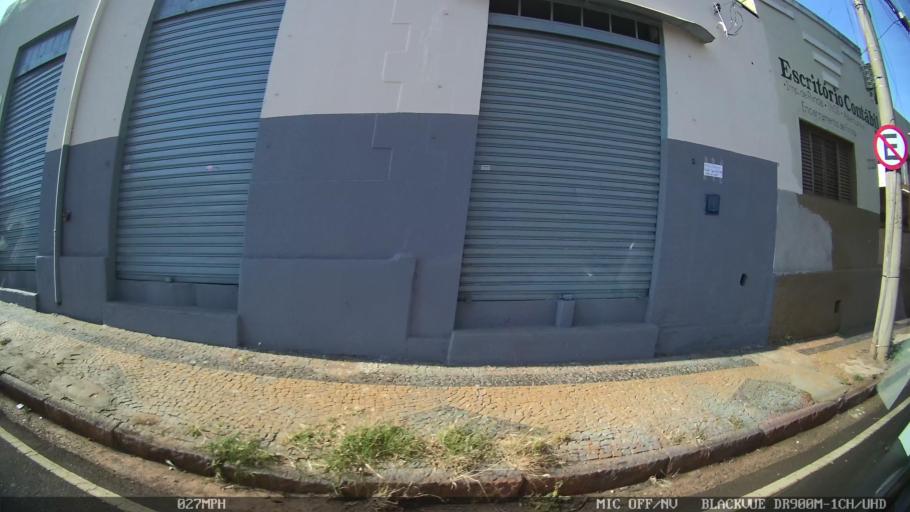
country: BR
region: Sao Paulo
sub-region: Sao Jose Do Rio Preto
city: Sao Jose do Rio Preto
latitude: -20.8048
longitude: -49.3835
